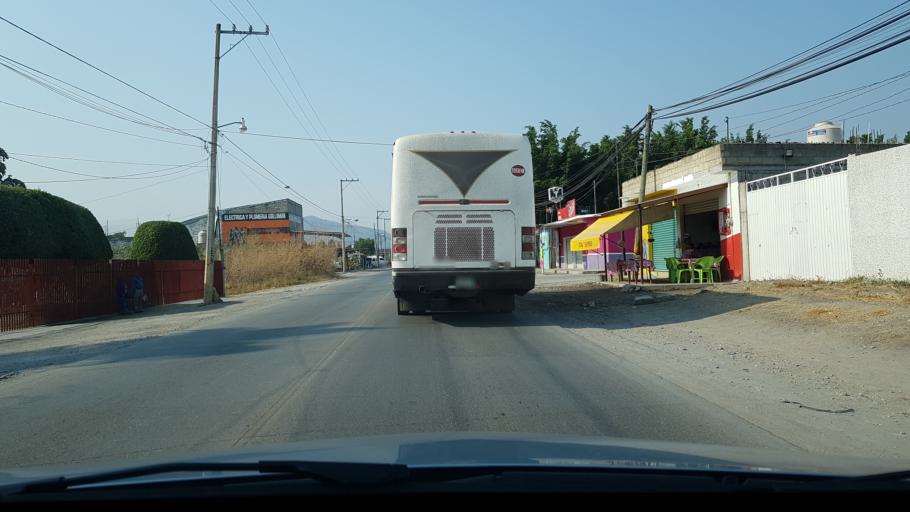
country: MX
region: Morelos
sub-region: Tlaquiltenango
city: Alfredo V. Bonfil (Chacampalco)
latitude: 18.6514
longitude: -99.1553
